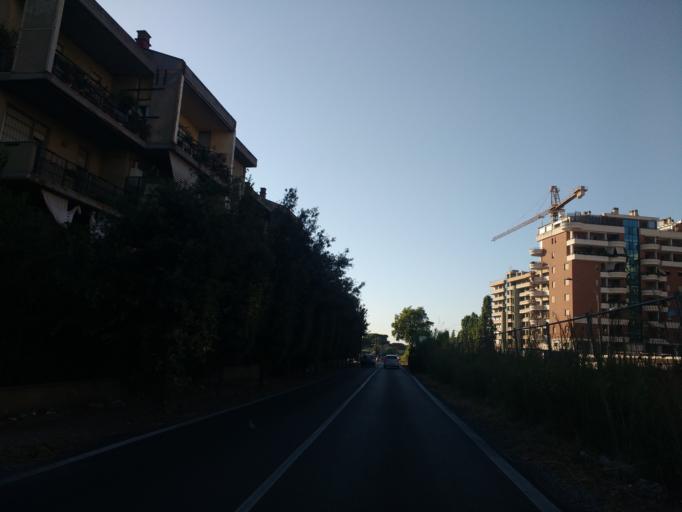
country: IT
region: Latium
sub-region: Citta metropolitana di Roma Capitale
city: Vitinia
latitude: 41.7712
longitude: 12.3731
